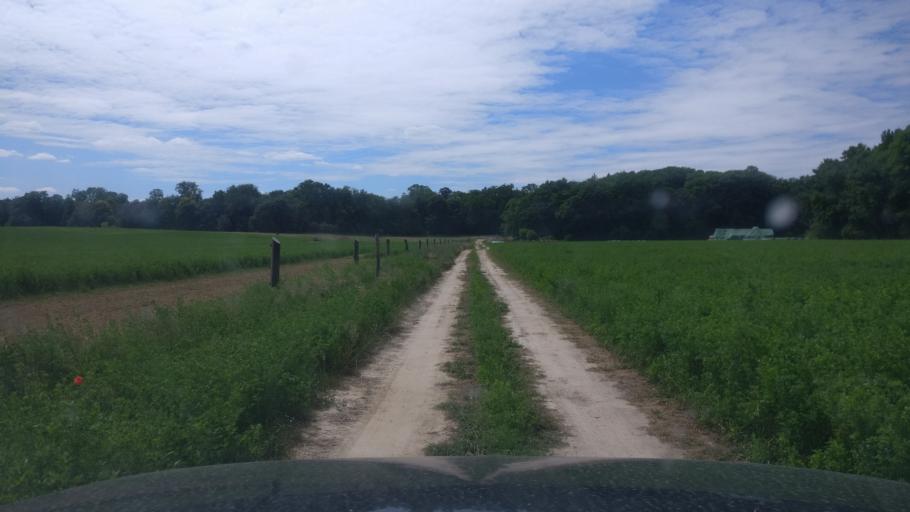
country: DE
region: Brandenburg
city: Briesen
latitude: 52.3920
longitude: 14.2845
